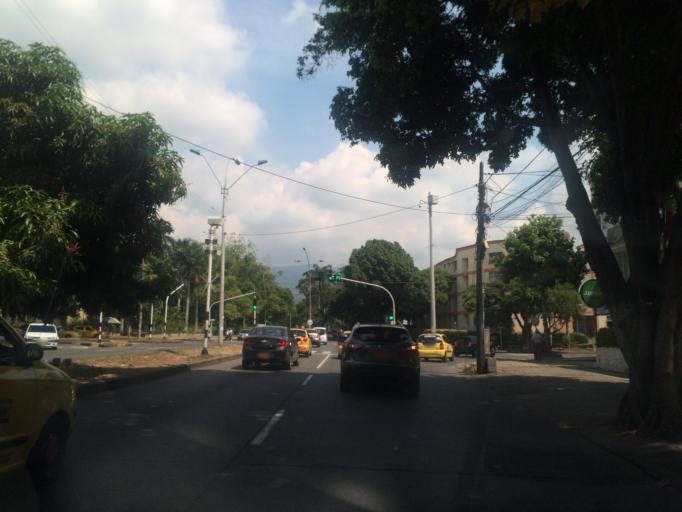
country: CO
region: Valle del Cauca
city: Cali
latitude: 3.4074
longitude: -76.5422
